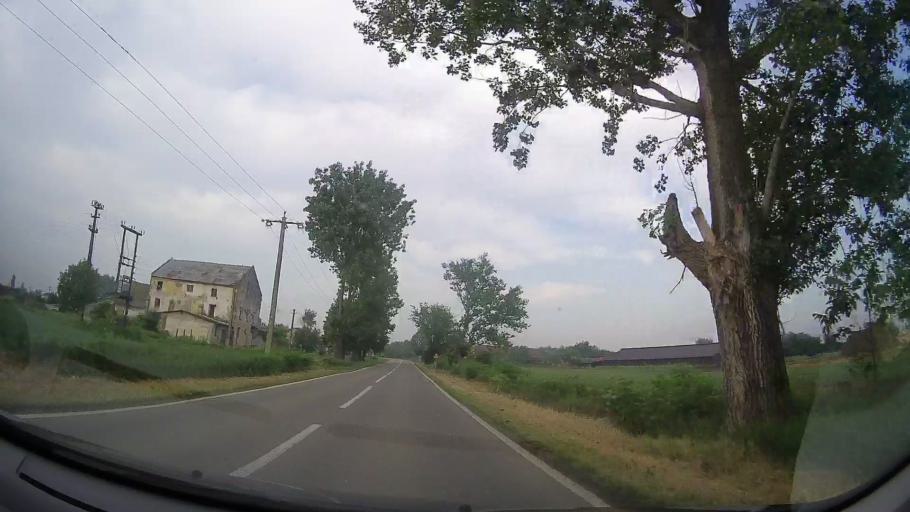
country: RO
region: Timis
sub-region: Comuna Parta
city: Parta
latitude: 45.6452
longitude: 21.1345
